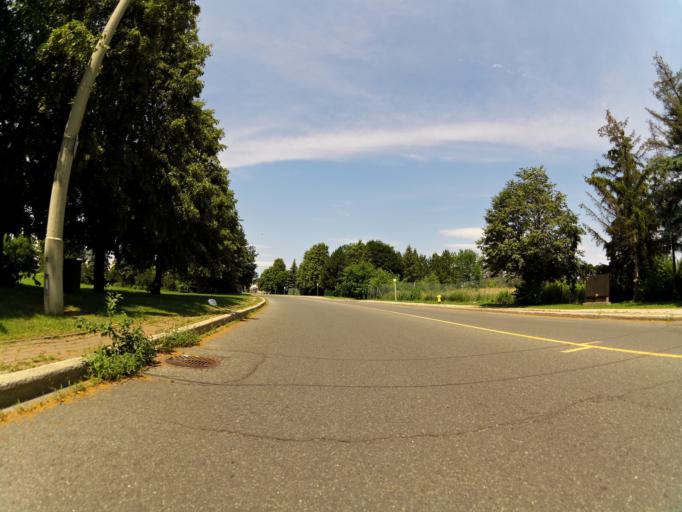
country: CA
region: Ontario
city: Ottawa
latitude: 45.3805
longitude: -75.6329
